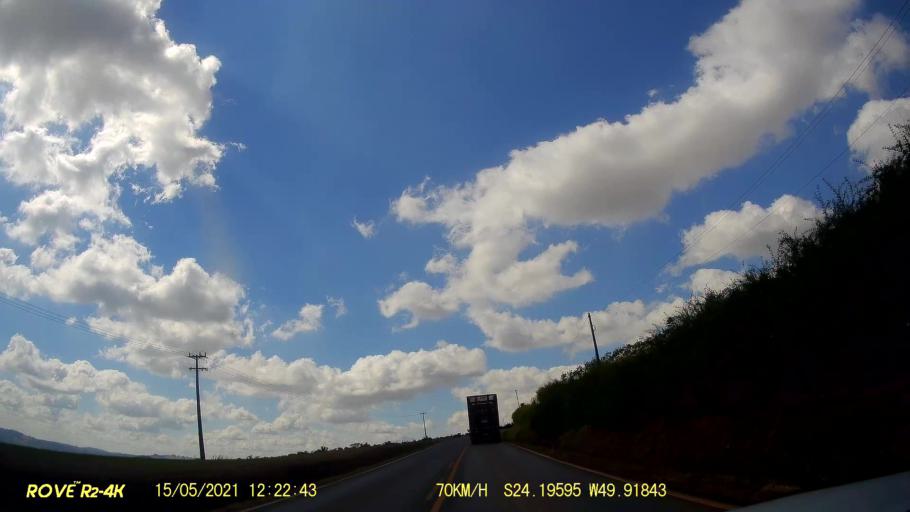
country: BR
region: Parana
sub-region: Jaguariaiva
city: Jaguariaiva
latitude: -24.1958
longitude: -49.9183
